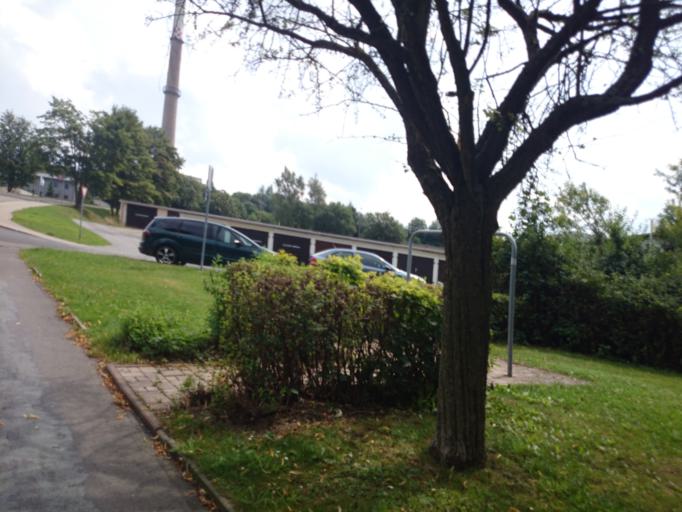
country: DE
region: Saxony
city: Brand-Erbisdorf
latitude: 50.8736
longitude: 13.3298
